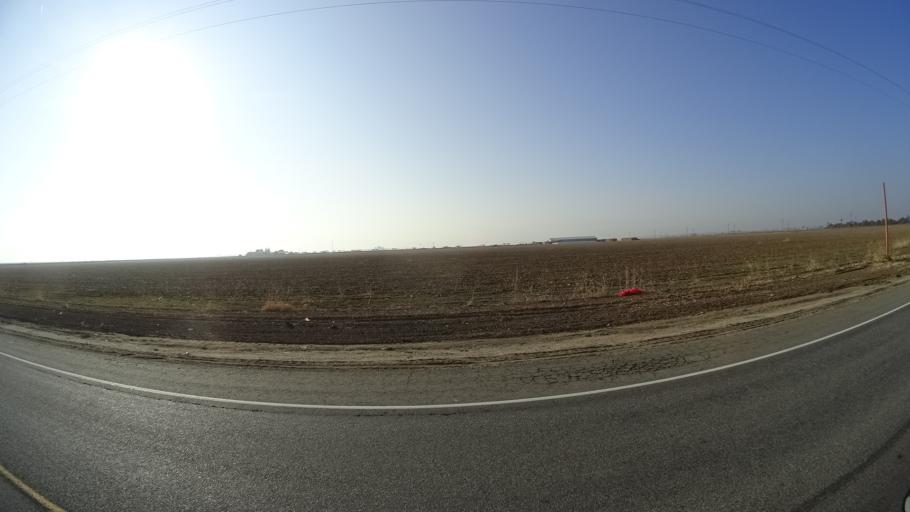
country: US
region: California
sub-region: Kern County
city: Greenfield
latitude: 35.2378
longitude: -118.9717
